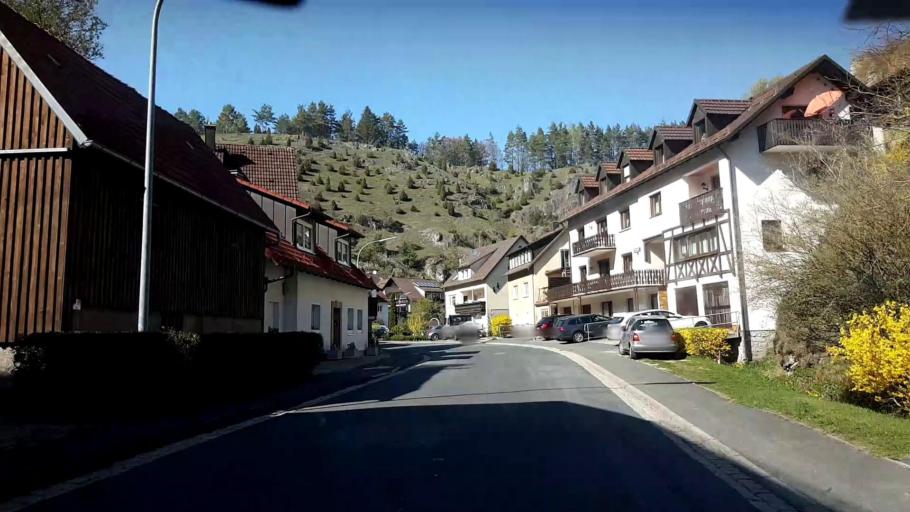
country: DE
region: Bavaria
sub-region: Upper Franconia
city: Pottenstein
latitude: 49.7736
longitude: 11.4127
